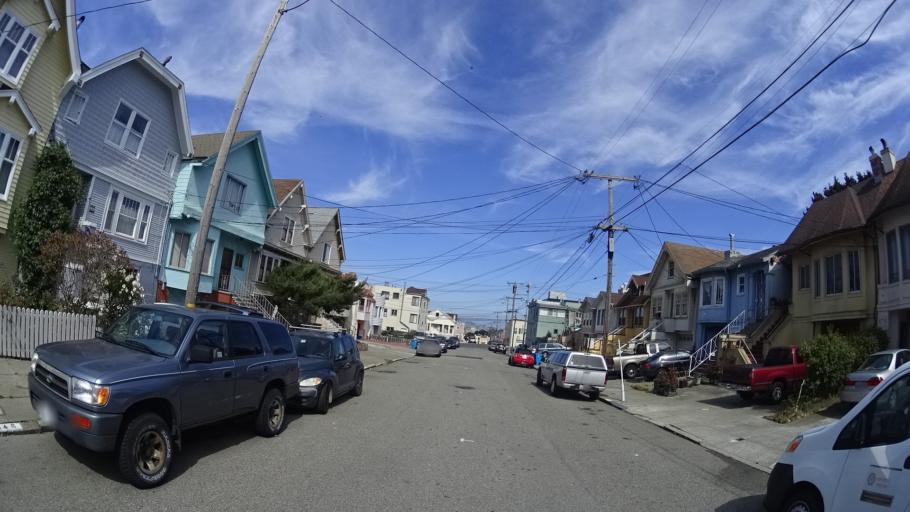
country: US
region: California
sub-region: San Mateo County
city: Daly City
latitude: 37.7091
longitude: -122.4547
